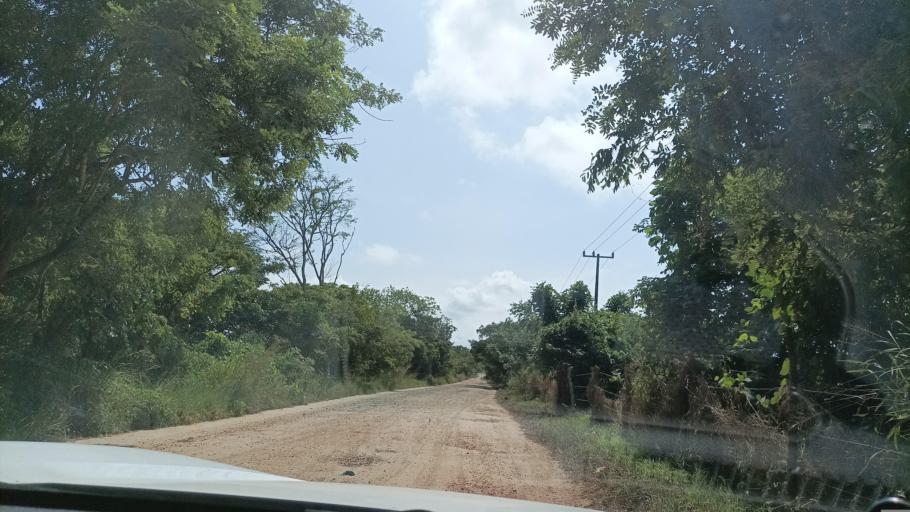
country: MX
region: Veracruz
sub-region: Chinameca
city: Chacalapa
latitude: 18.1275
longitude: -94.6550
